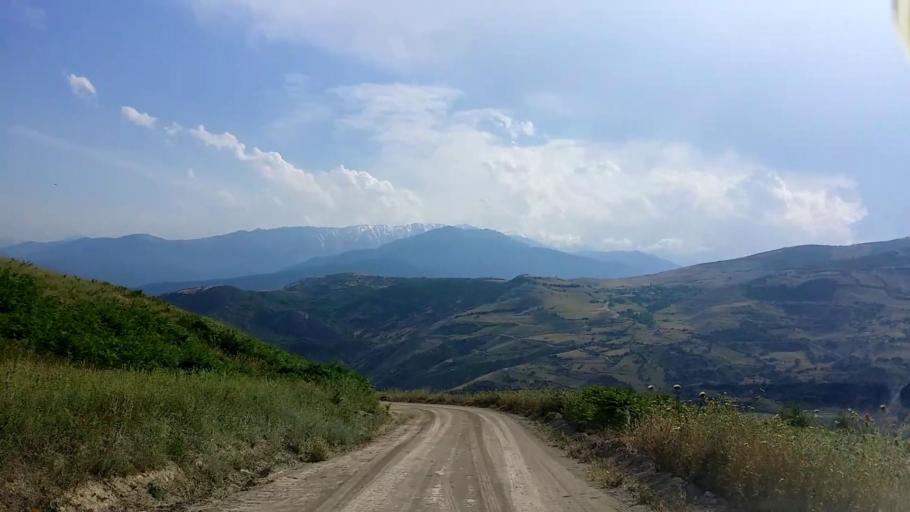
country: IR
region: Mazandaran
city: Chalus
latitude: 36.5497
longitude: 51.2956
